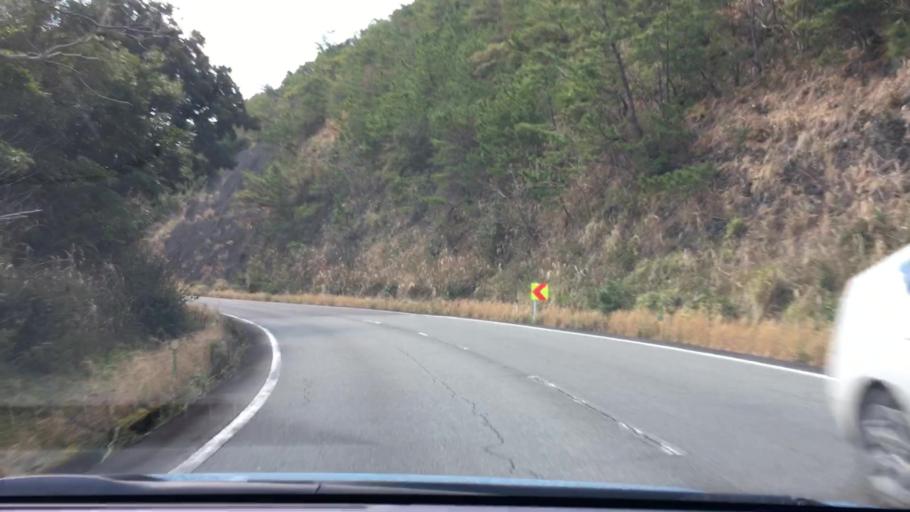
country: JP
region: Mie
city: Toba
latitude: 34.4419
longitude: 136.9110
